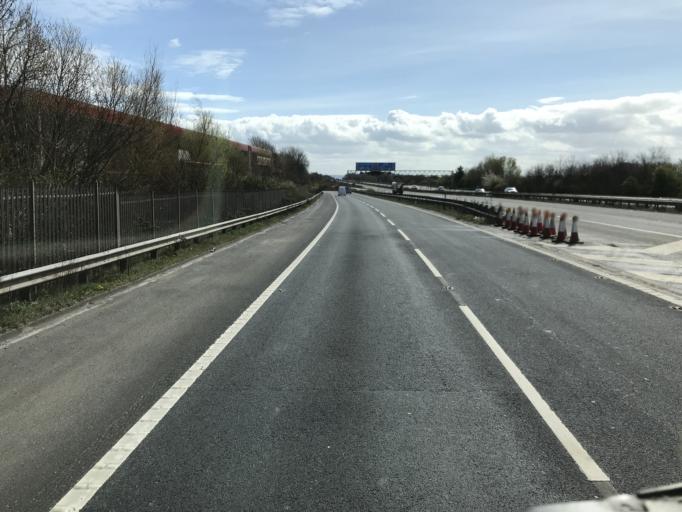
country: GB
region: England
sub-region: Knowsley
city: Huyton
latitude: 53.4042
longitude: -2.8133
